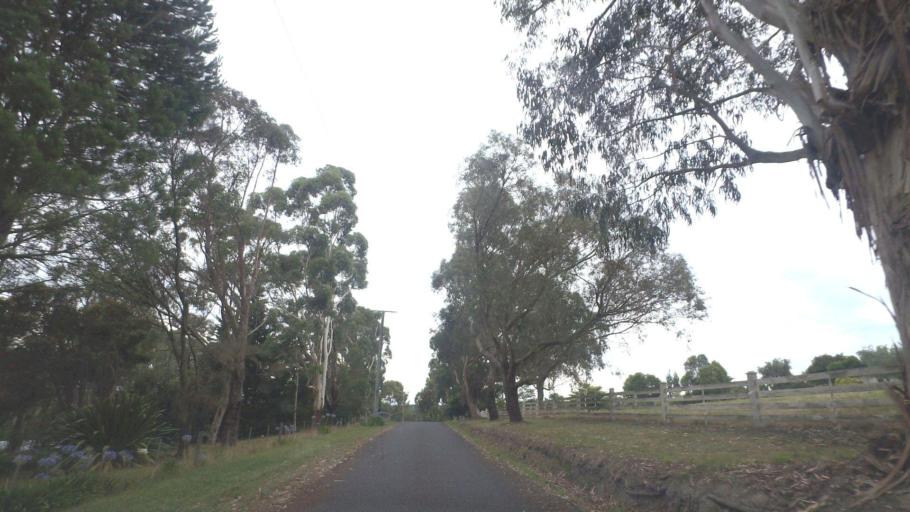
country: AU
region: Victoria
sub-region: Yarra Ranges
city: Mount Evelyn
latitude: -37.7698
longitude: 145.4000
